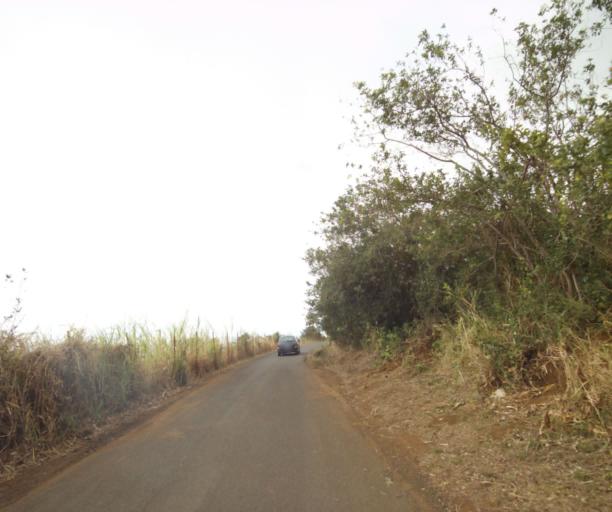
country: RE
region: Reunion
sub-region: Reunion
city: Saint-Paul
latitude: -21.0270
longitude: 55.3012
